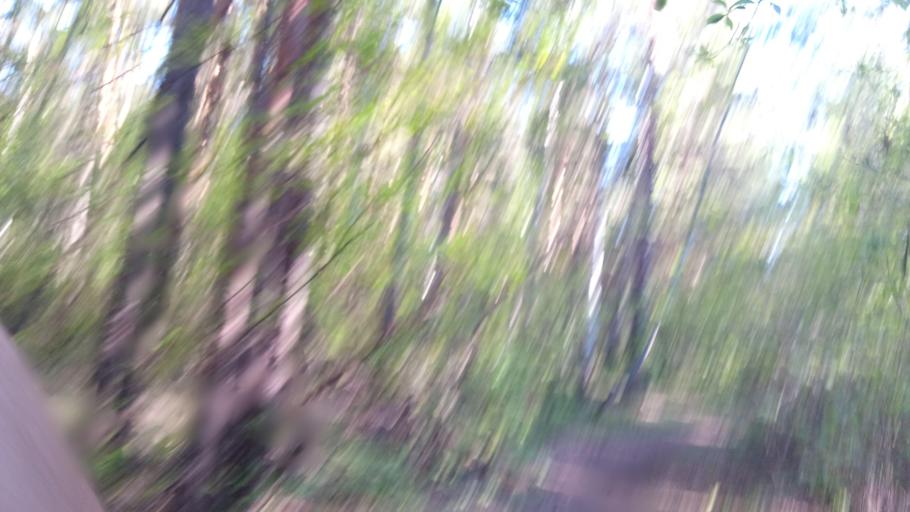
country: RU
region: Chelyabinsk
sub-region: Gorod Chelyabinsk
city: Chelyabinsk
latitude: 55.1520
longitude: 61.3484
